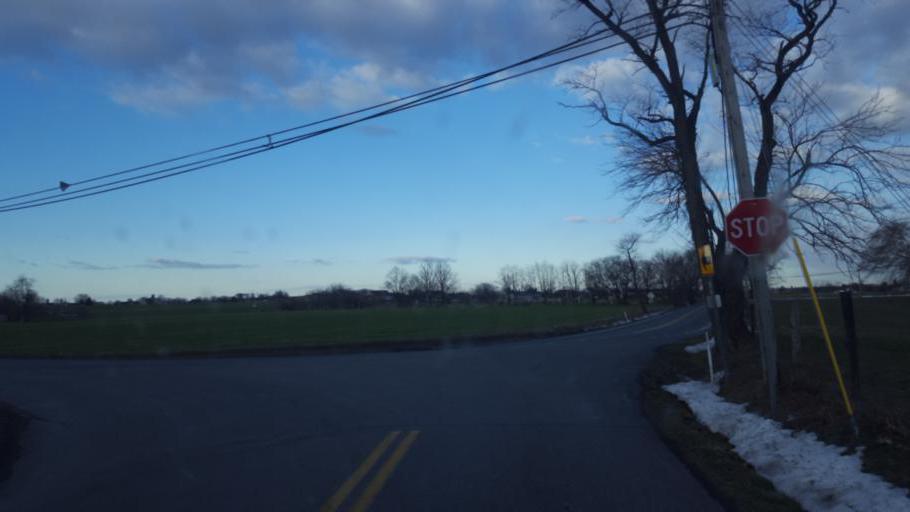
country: US
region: Pennsylvania
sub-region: Lancaster County
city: New Holland
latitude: 40.0679
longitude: -76.0679
